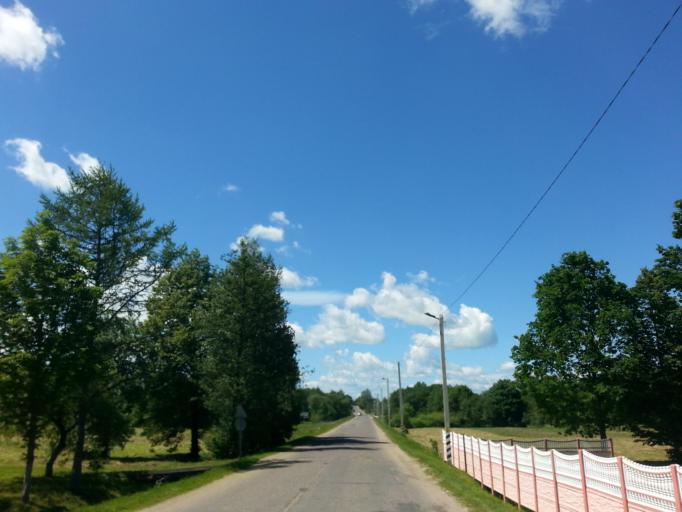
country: BY
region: Vitebsk
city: Mosar
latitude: 55.2101
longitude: 27.5568
